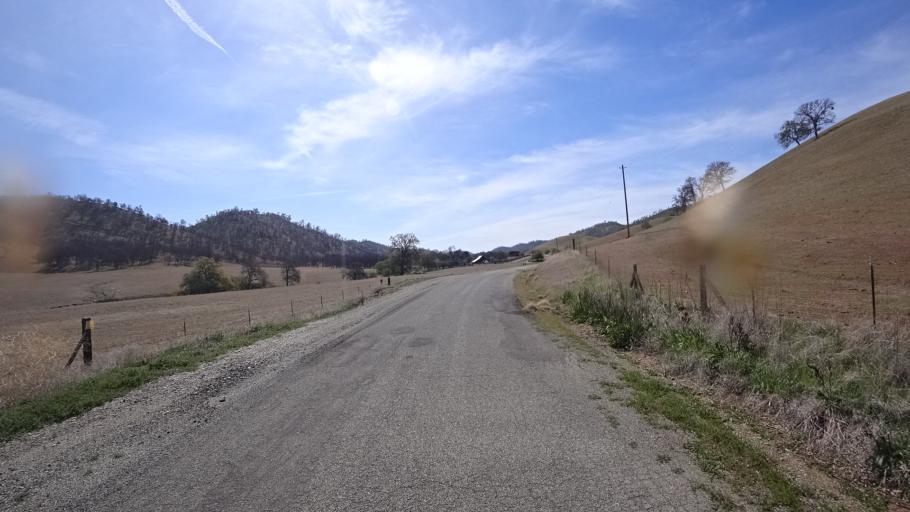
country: US
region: California
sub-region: Glenn County
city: Willows
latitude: 39.4878
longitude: -122.4529
